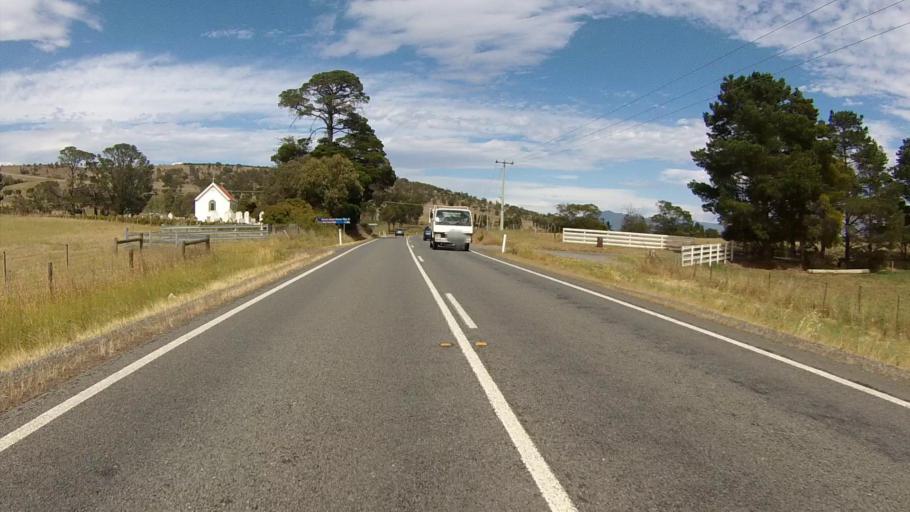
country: AU
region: Tasmania
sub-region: Brighton
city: Old Beach
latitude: -42.6908
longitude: 147.3456
